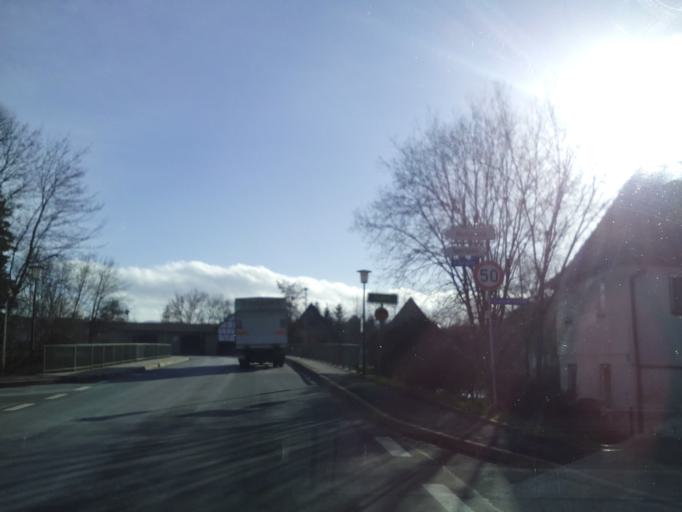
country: DE
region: Bavaria
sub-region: Upper Franconia
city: Marktzeuln
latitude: 50.1664
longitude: 11.1711
